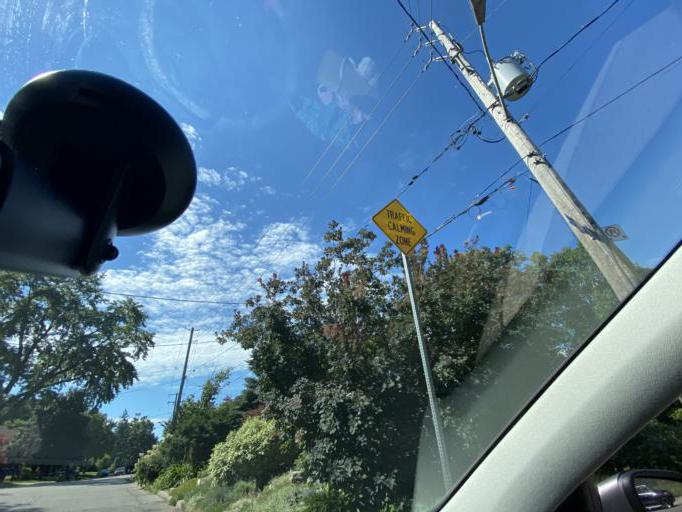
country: CA
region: Ontario
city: Etobicoke
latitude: 43.6596
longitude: -79.4926
